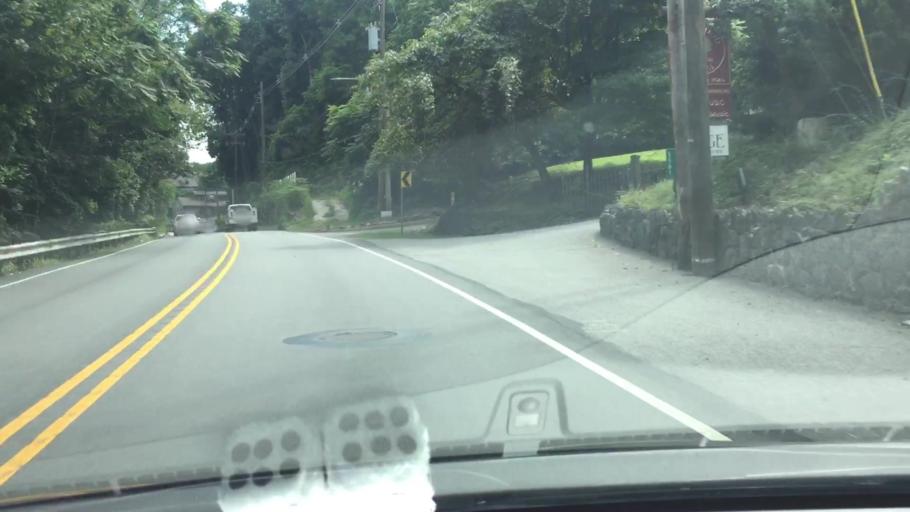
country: US
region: Pennsylvania
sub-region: Delaware County
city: Village Green-Green Ridge
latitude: 39.8862
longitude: -75.4312
